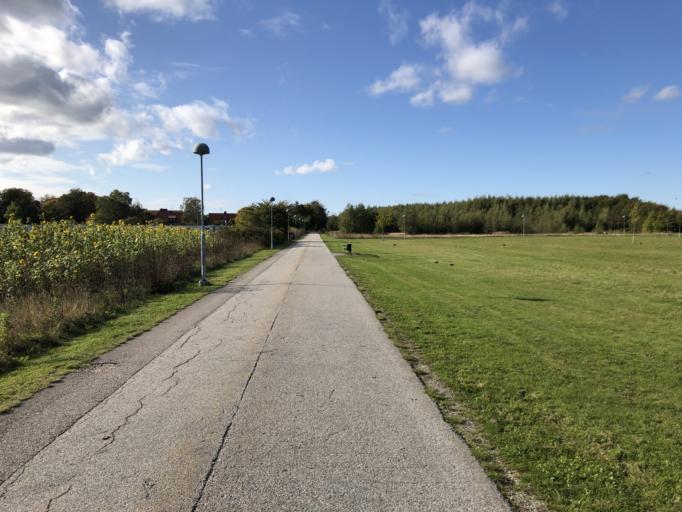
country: SE
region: Skane
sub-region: Lunds Kommun
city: Lund
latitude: 55.6873
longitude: 13.2136
